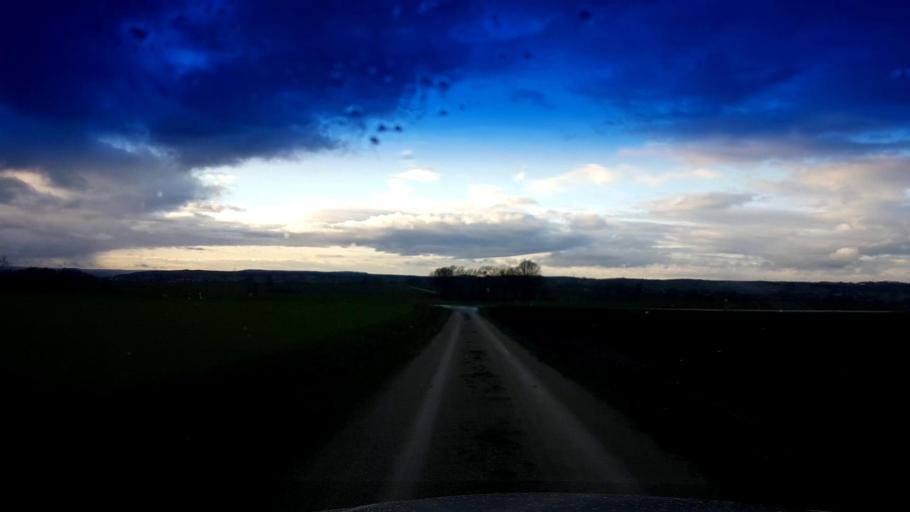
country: DE
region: Bavaria
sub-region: Upper Franconia
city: Schesslitz
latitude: 49.9492
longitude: 11.0213
